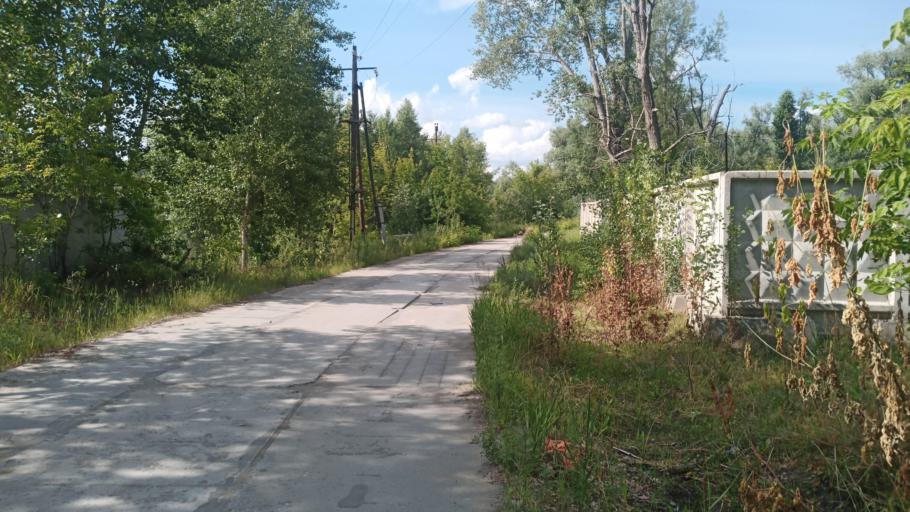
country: RU
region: Altai Krai
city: Zaton
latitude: 53.3397
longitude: 83.8060
